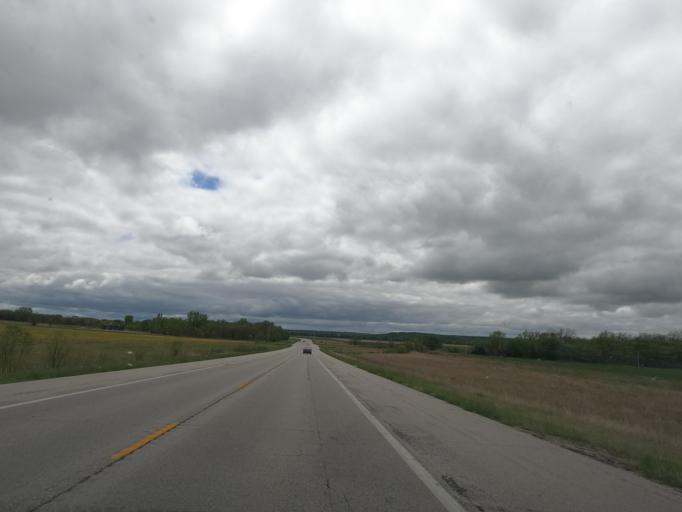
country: US
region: Kansas
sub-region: Wilson County
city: Neodesha
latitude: 37.4608
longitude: -95.7239
